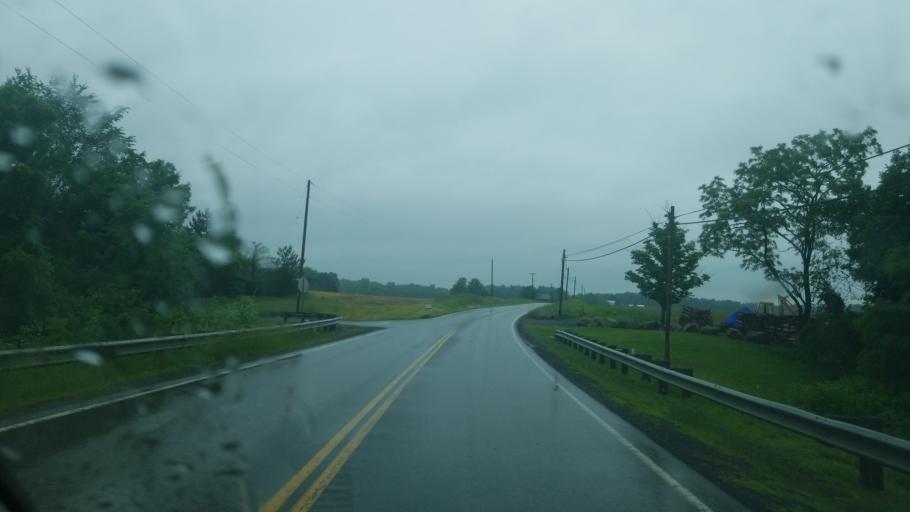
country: US
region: Ohio
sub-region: Huron County
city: Greenwich
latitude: 40.9398
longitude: -82.5516
